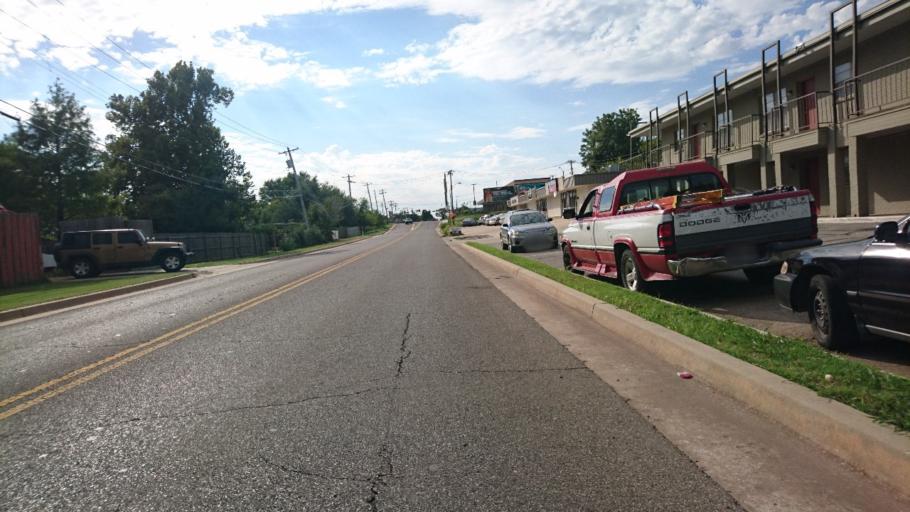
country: US
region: Oklahoma
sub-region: Oklahoma County
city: Nichols Hills
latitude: 35.5076
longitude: -97.5624
